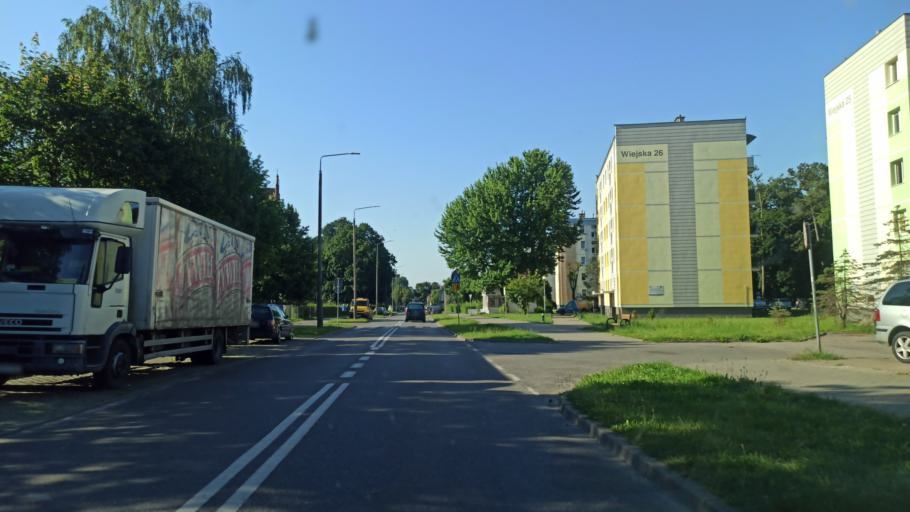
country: PL
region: Warmian-Masurian Voivodeship
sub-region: Powiat elblaski
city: Elblag
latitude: 54.1867
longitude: 19.3950
